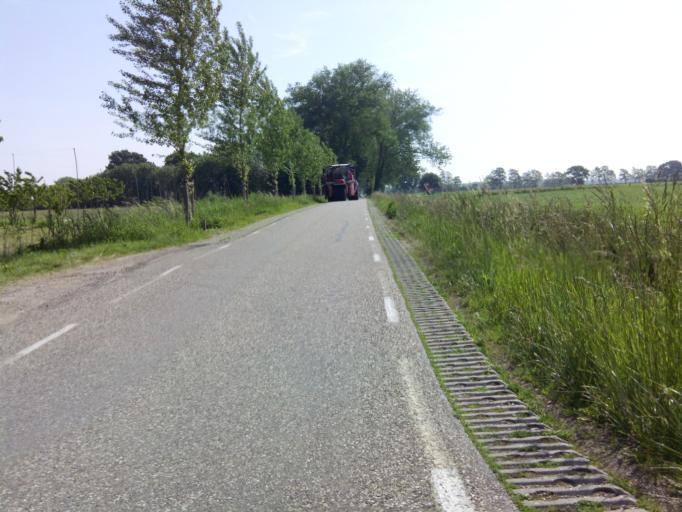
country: NL
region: Utrecht
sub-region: Gemeente Wijk bij Duurstede
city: Wijk bij Duurstede
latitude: 51.9841
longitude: 5.3596
